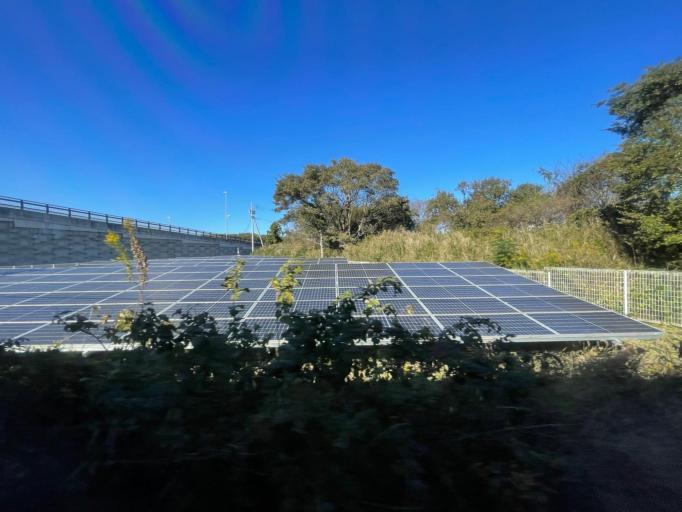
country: JP
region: Chiba
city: Asahi
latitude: 35.7207
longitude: 140.6183
